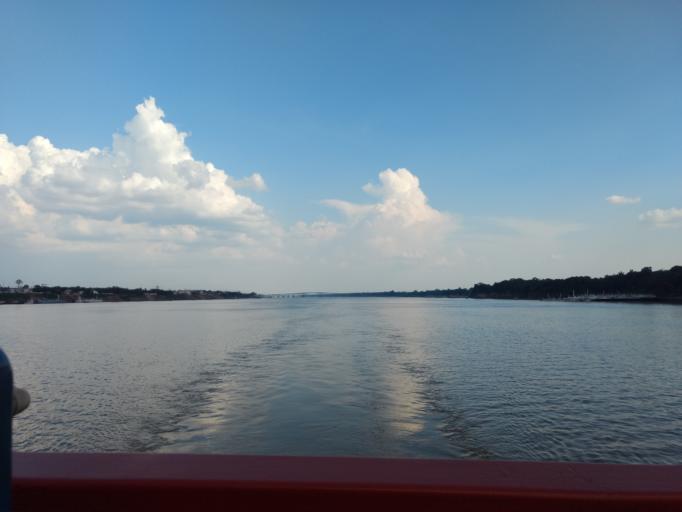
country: BR
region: Rondonia
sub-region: Porto Velho
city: Porto Velho
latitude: -8.6936
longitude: -63.9220
